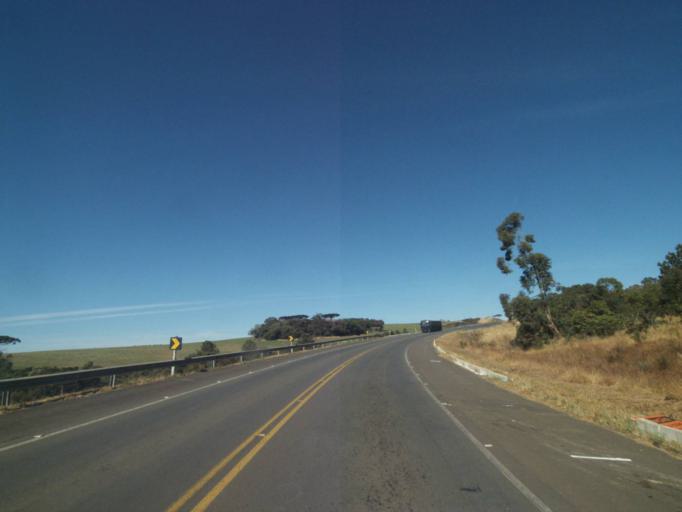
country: BR
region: Parana
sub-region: Tibagi
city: Tibagi
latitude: -24.7916
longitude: -50.4660
